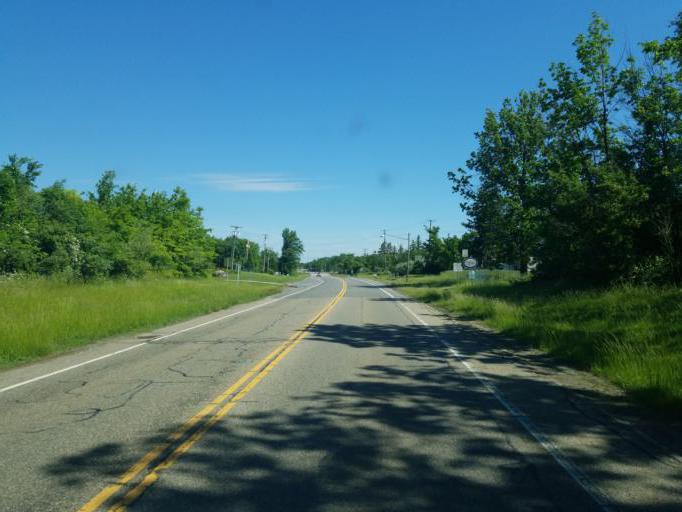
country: US
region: Ohio
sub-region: Summit County
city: Boston Heights
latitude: 41.2259
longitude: -81.4906
